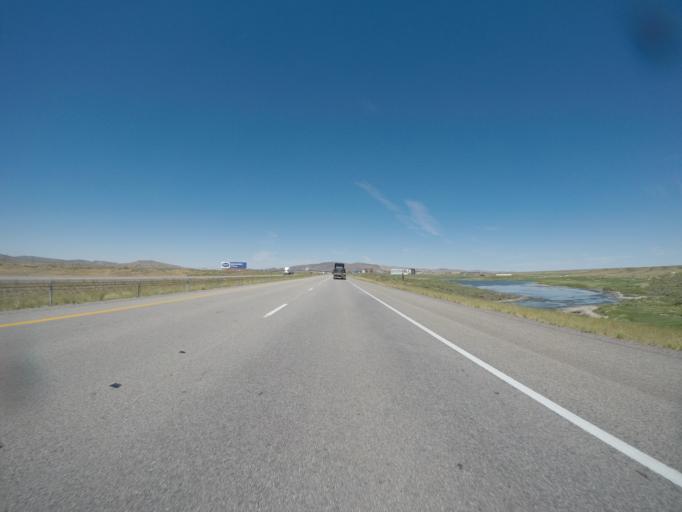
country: US
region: Wyoming
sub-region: Carbon County
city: Rawlins
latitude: 41.7861
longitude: -107.1802
